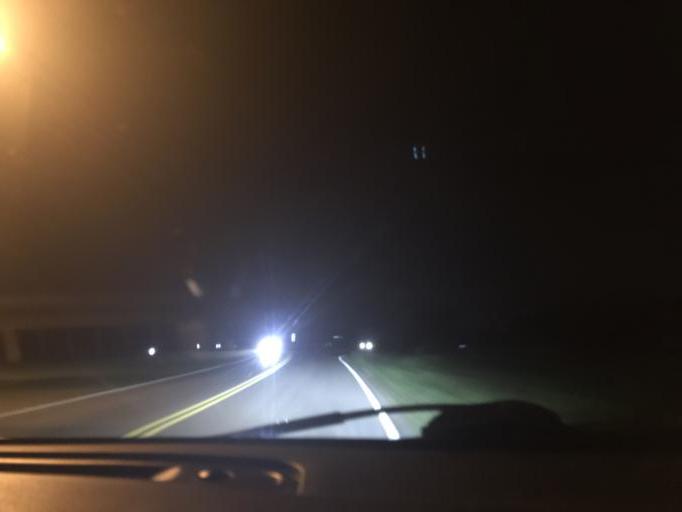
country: US
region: South Carolina
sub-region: Cherokee County
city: East Gaffney
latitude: 35.1208
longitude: -81.6559
